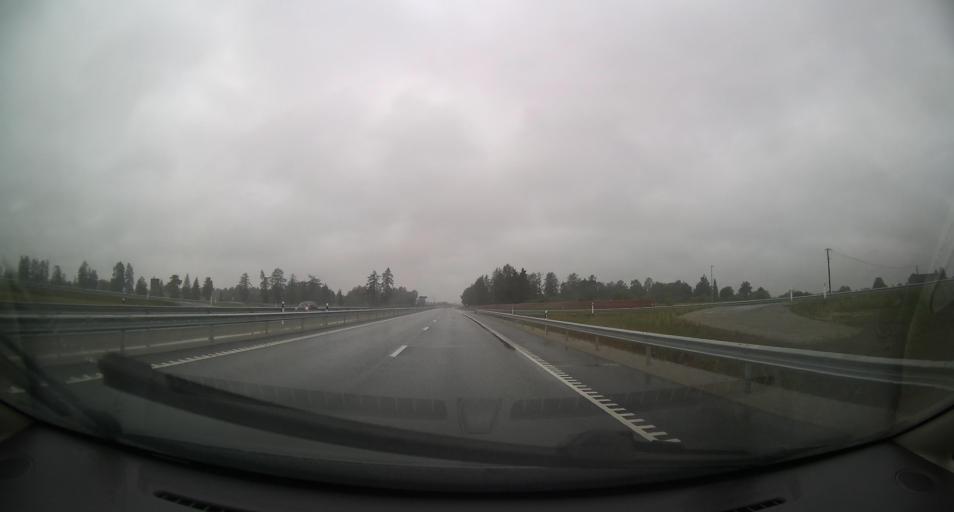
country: EE
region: Laeaene-Virumaa
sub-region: Kadrina vald
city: Kadrina
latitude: 59.4389
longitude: 26.1453
